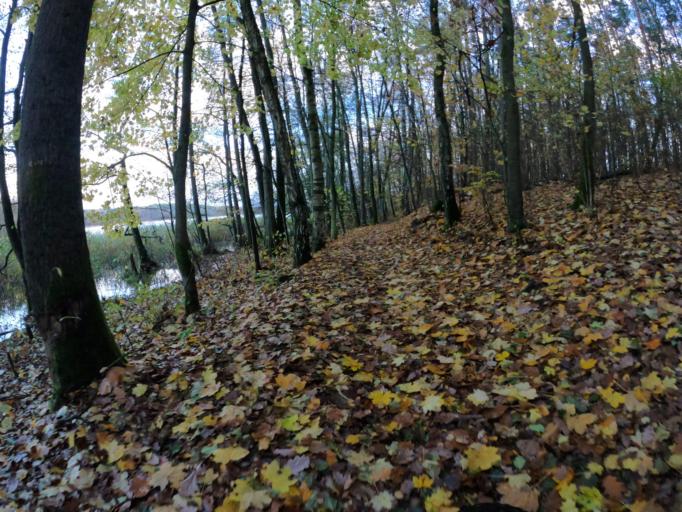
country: PL
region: West Pomeranian Voivodeship
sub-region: Powiat walecki
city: Tuczno
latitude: 53.1887
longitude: 16.1694
